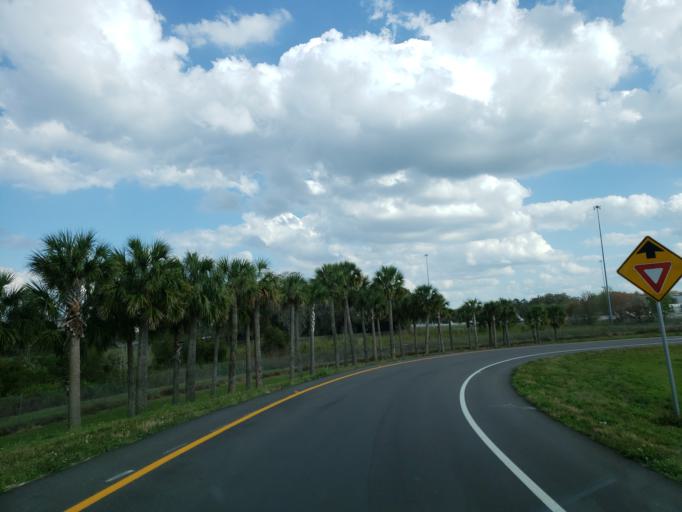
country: US
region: Florida
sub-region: Hillsborough County
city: East Lake-Orient Park
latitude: 27.9976
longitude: -82.3559
